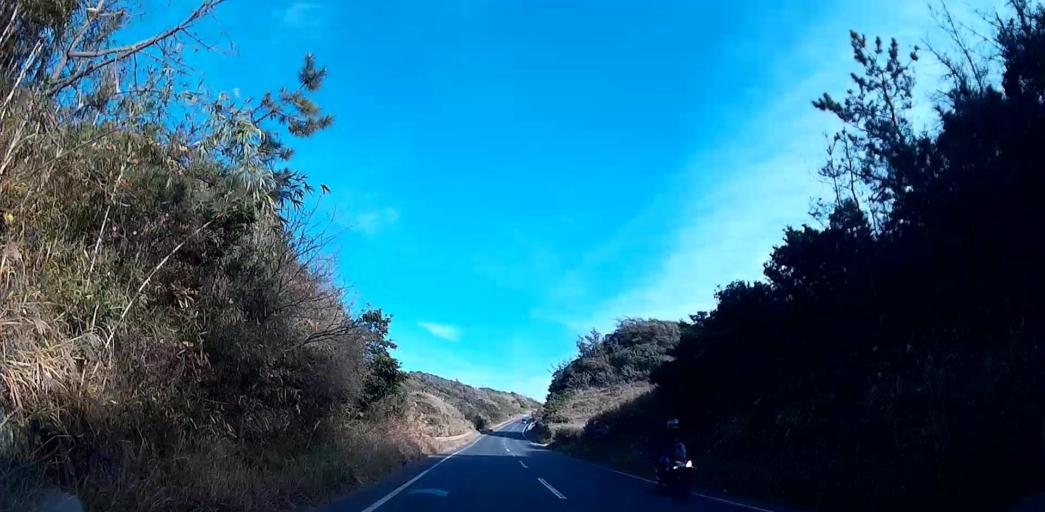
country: JP
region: Chiba
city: Hasaki
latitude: 35.7140
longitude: 140.8145
